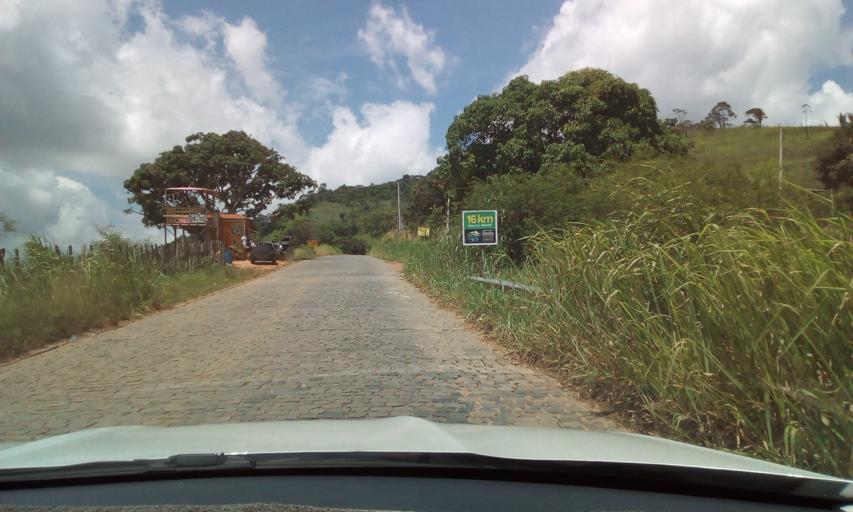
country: BR
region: Pernambuco
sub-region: Bonito
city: Bonito
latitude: -8.4906
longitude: -35.7253
